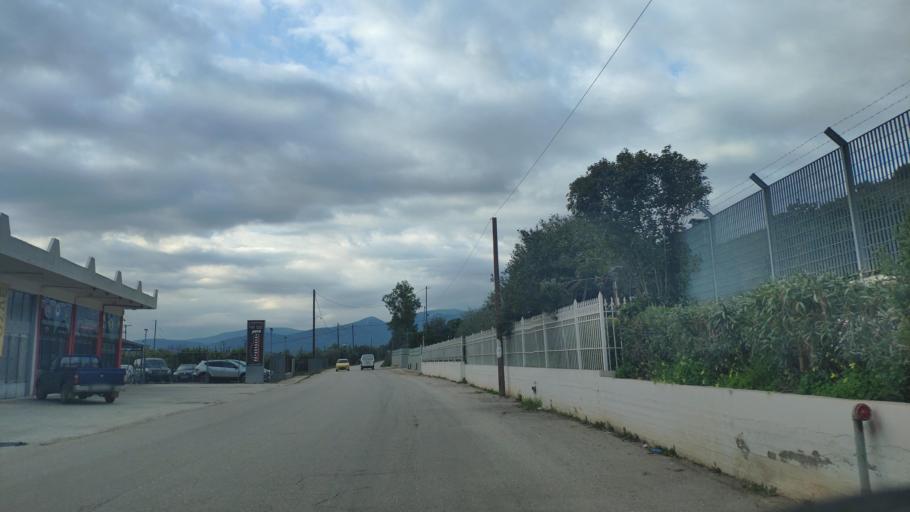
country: GR
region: Peloponnese
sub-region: Nomos Argolidos
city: Argos
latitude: 37.6188
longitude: 22.7115
